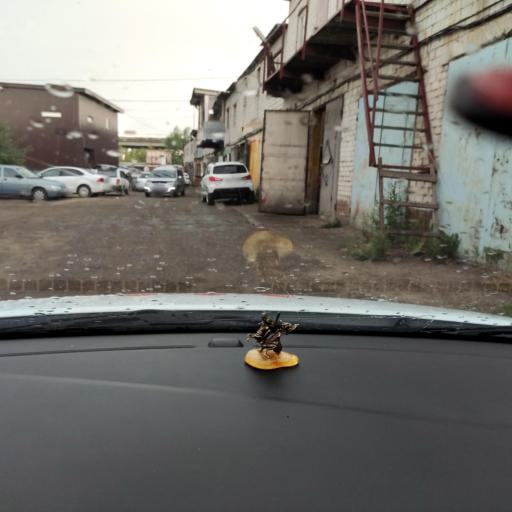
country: RU
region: Tatarstan
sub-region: Gorod Kazan'
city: Kazan
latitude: 55.8477
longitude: 49.1356
